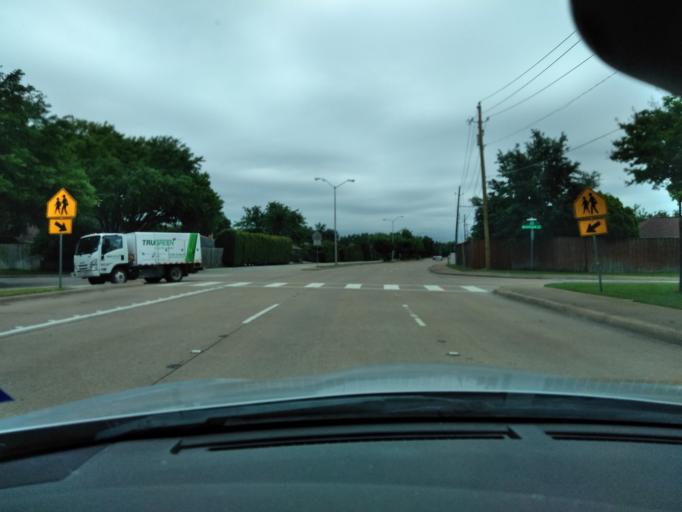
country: US
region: Texas
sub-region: Dallas County
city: Addison
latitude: 32.9751
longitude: -96.7841
